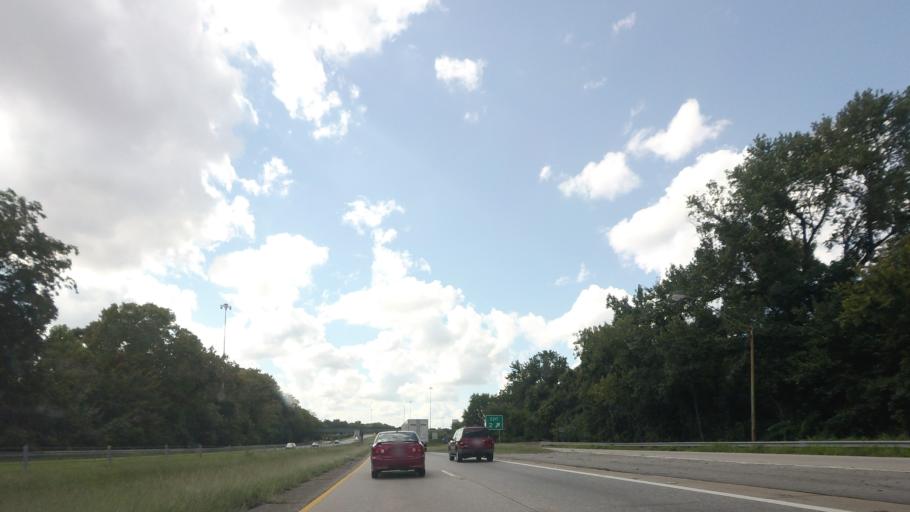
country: US
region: Georgia
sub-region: Bibb County
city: Macon
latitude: 32.8381
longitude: -83.6157
